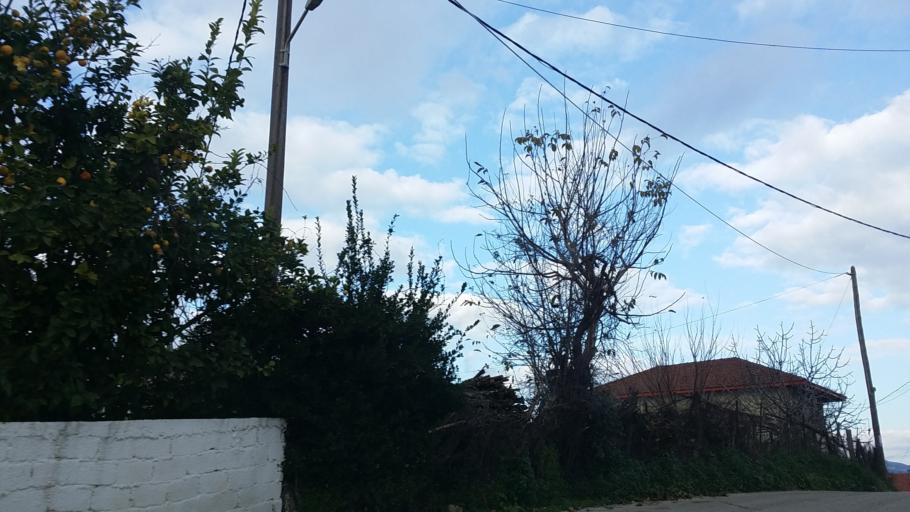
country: GR
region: West Greece
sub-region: Nomos Aitolias kai Akarnanias
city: Katouna
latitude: 38.7857
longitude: 21.1110
